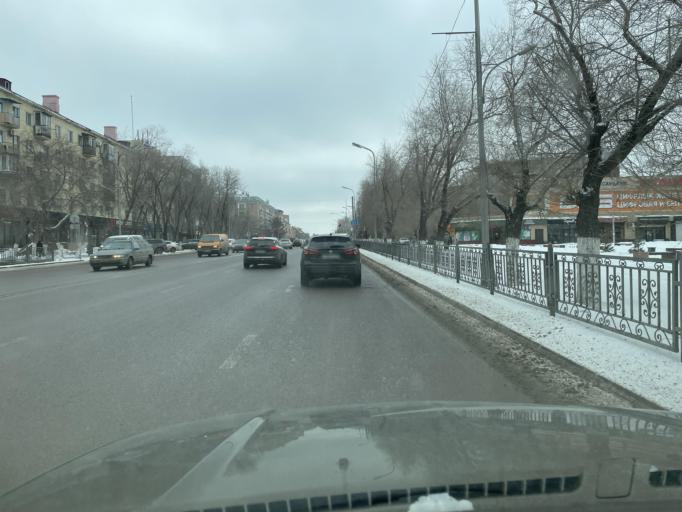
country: KZ
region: Qaraghandy
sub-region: Qaraghandy Qalasy
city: Karagandy
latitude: 49.8029
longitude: 73.0877
